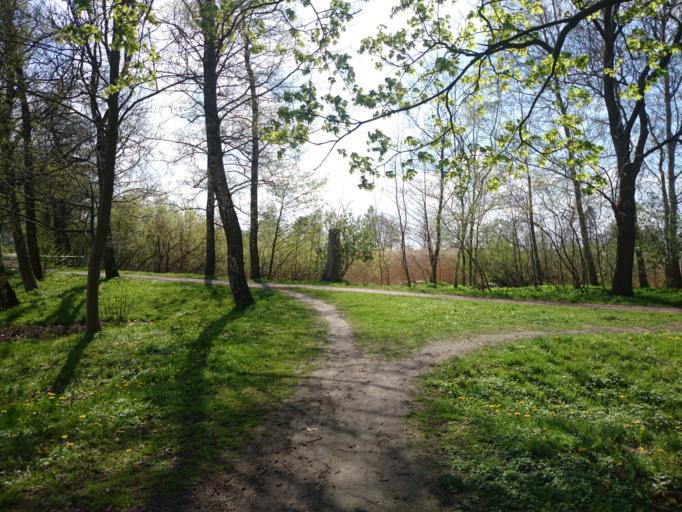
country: DE
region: Mecklenburg-Vorpommern
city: Broderstorf
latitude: 54.0704
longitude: 12.3341
